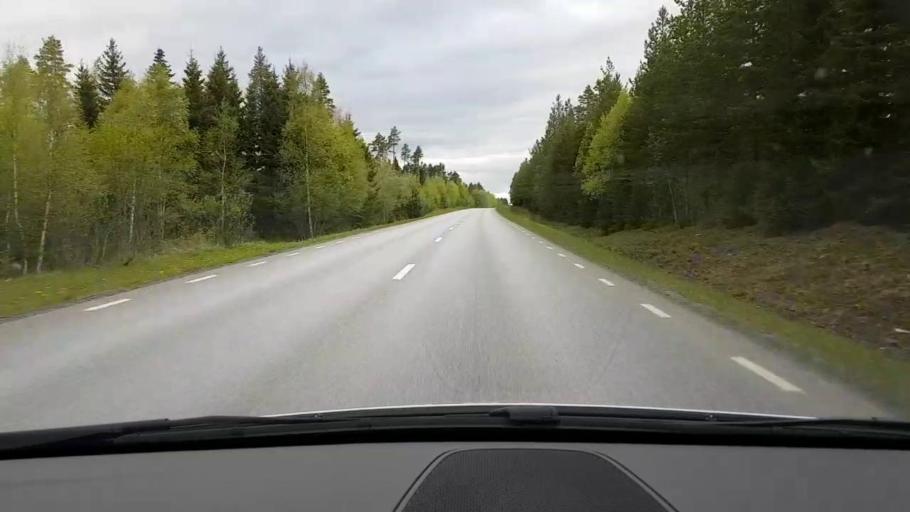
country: SE
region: Jaemtland
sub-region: Krokoms Kommun
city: Valla
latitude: 63.2629
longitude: 13.9722
